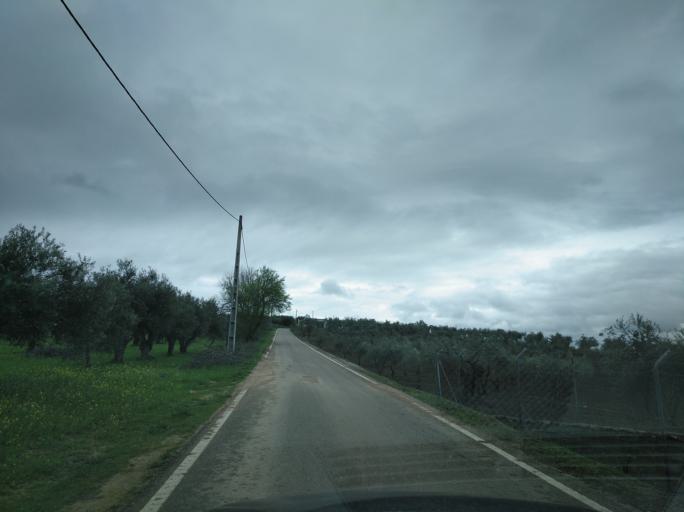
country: PT
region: Portalegre
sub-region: Campo Maior
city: Campo Maior
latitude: 38.9941
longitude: -7.0496
